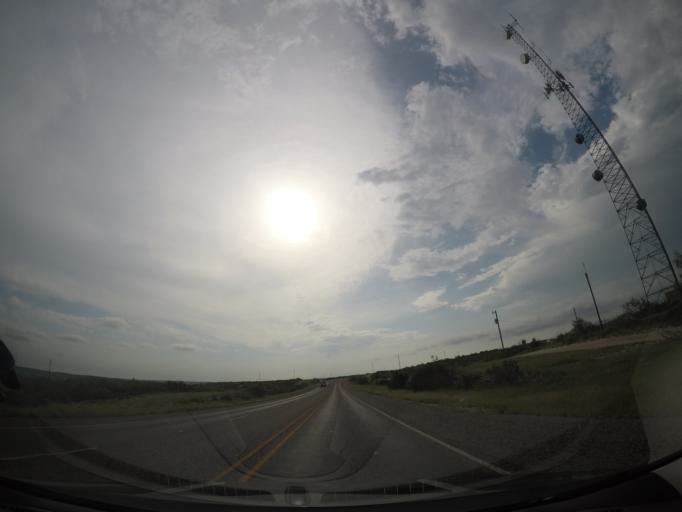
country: US
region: Texas
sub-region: Terrell County
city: Sanderson
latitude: 29.8315
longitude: -101.6358
